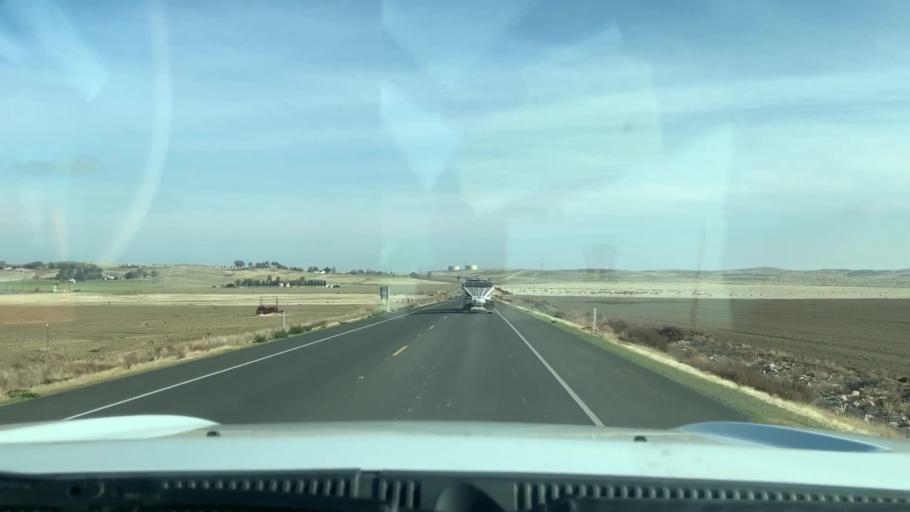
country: US
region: California
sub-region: Fresno County
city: Coalinga
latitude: 36.1971
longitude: -120.3314
